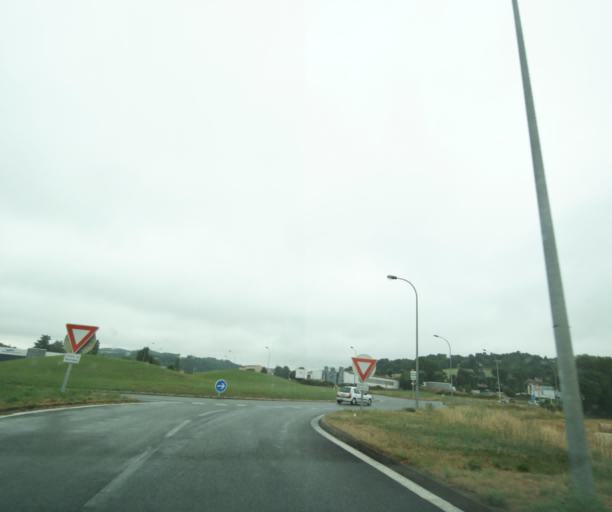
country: FR
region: Midi-Pyrenees
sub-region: Departement du Tarn
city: Arthes
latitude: 43.9640
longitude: 2.1830
